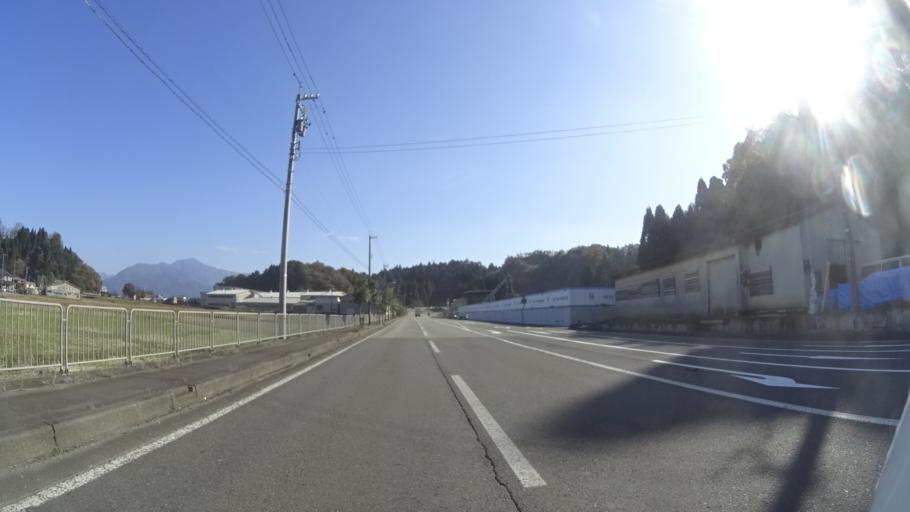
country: JP
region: Fukui
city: Ono
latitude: 35.9858
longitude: 136.4764
